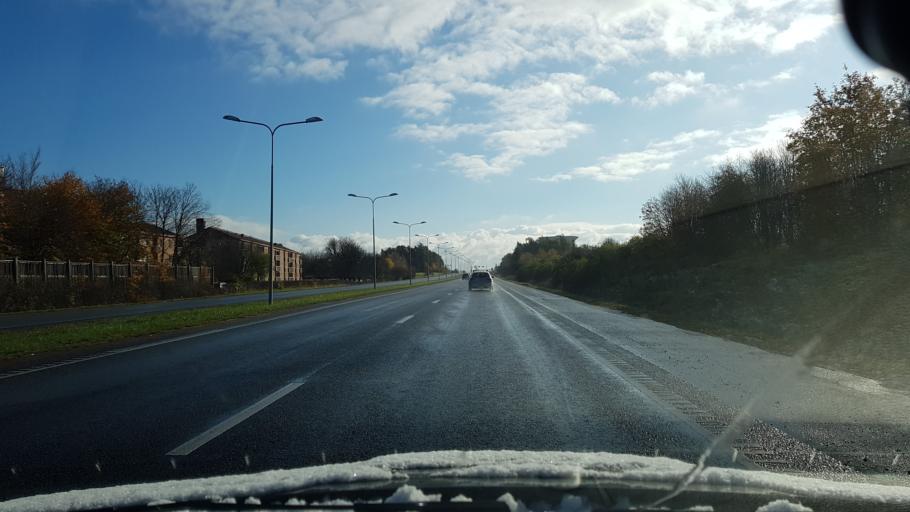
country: SE
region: Uppsala
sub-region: Uppsala Kommun
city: Uppsala
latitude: 59.8630
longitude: 17.6694
